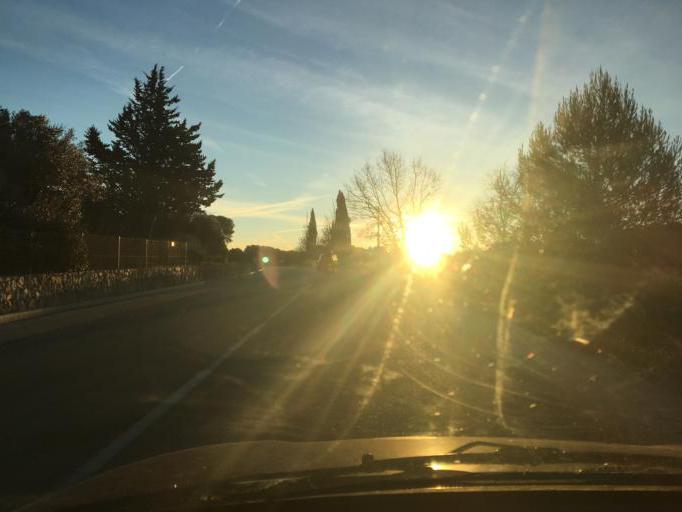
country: FR
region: Provence-Alpes-Cote d'Azur
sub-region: Departement du Var
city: Taradeau
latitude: 43.4653
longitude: 6.3944
